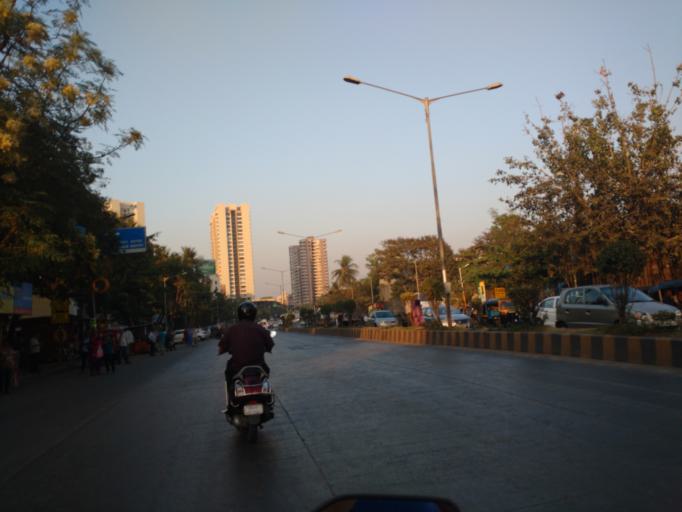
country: IN
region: Maharashtra
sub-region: Mumbai Suburban
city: Borivli
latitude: 19.2135
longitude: 72.8369
